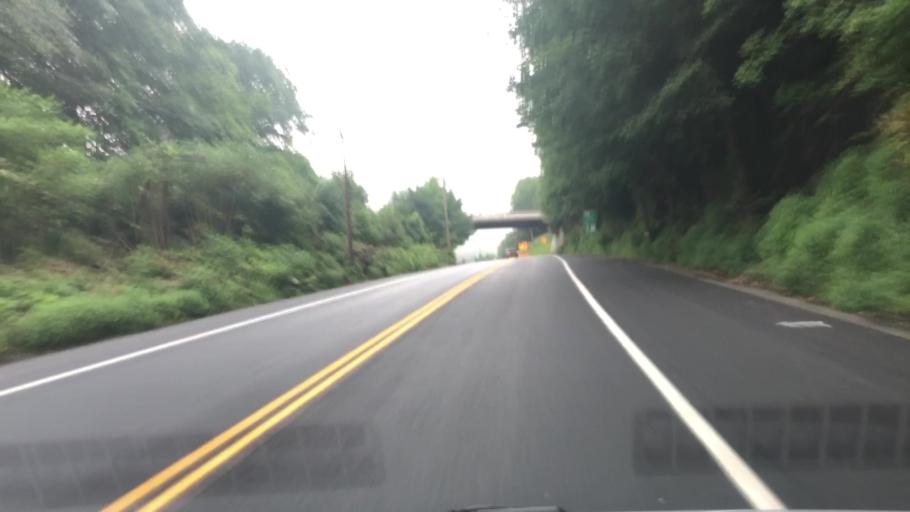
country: US
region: Massachusetts
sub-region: Franklin County
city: Shelburne Falls
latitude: 42.6162
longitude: -72.7429
